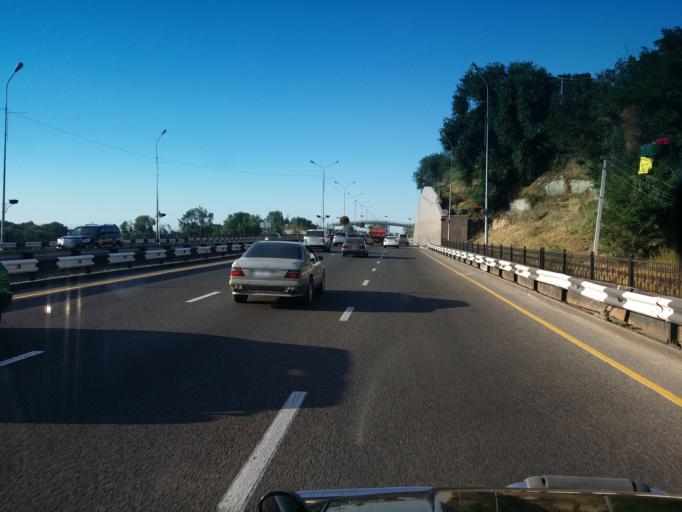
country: KZ
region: Almaty Qalasy
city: Almaty
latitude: 43.2314
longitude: 76.9688
